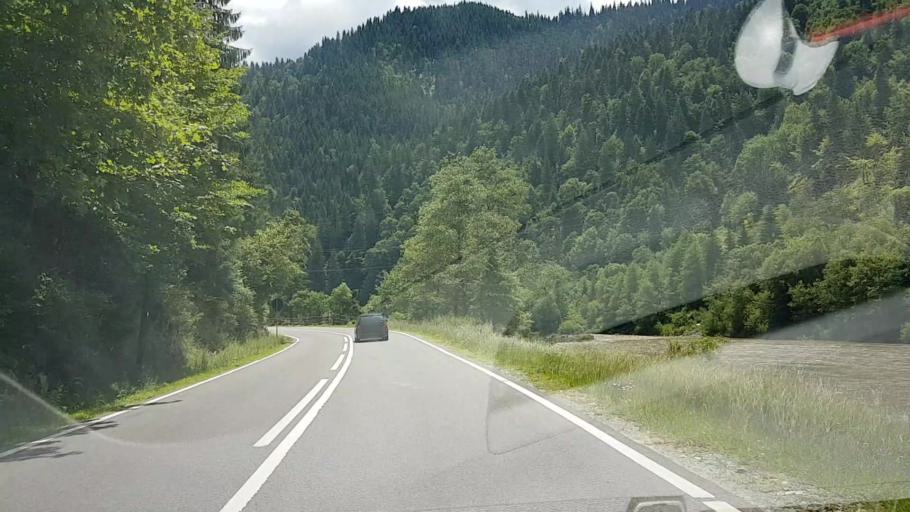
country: RO
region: Suceava
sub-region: Comuna Brosteni
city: Brosteni
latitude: 47.2599
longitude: 25.6689
